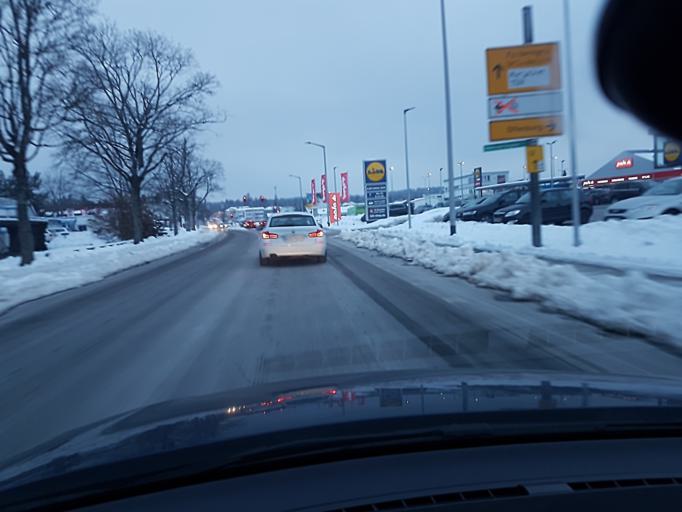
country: DE
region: Baden-Wuerttemberg
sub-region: Freiburg Region
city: Monchweiler
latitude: 48.0679
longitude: 8.4505
